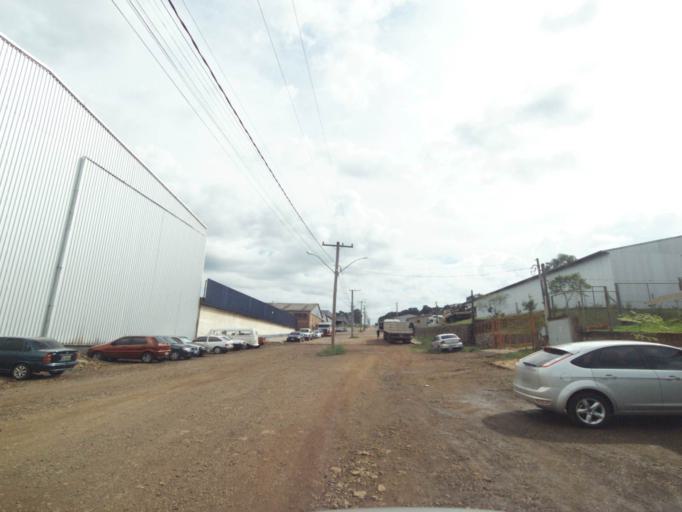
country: BR
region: Rio Grande do Sul
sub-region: Lagoa Vermelha
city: Lagoa Vermelha
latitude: -28.2314
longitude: -51.5153
